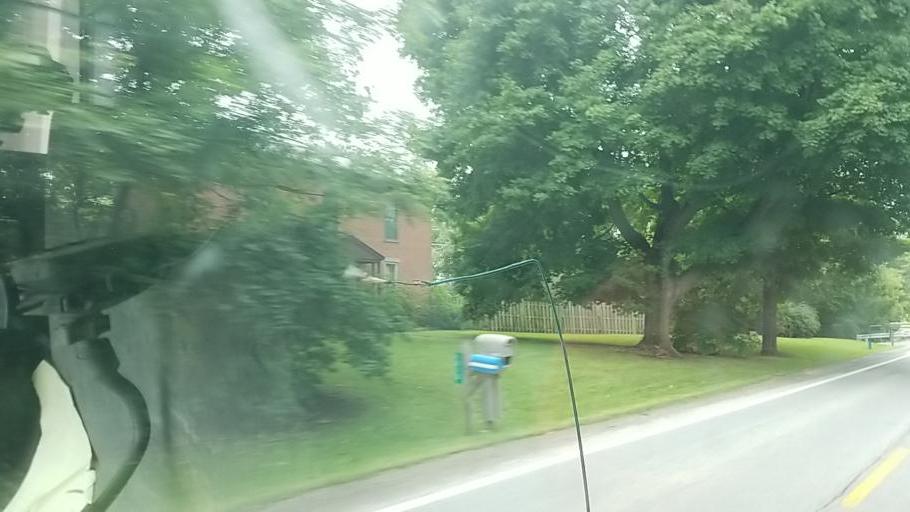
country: US
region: Ohio
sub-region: Pickaway County
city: Commercial Point
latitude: 39.8258
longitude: -83.0365
